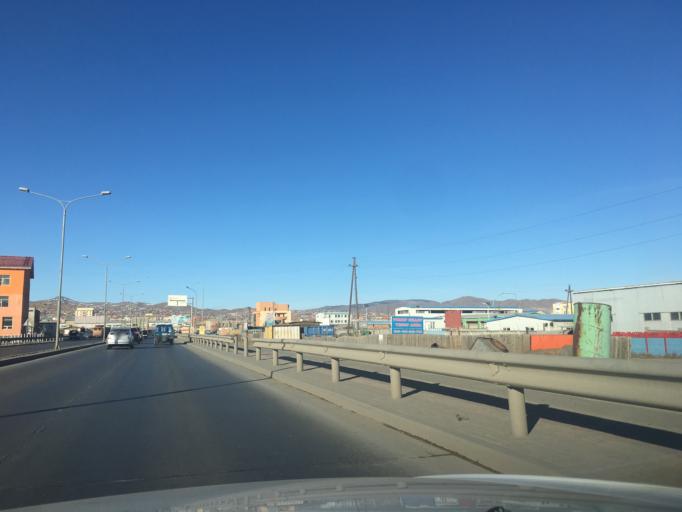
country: MN
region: Ulaanbaatar
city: Ulaanbaatar
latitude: 47.9038
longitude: 106.7858
